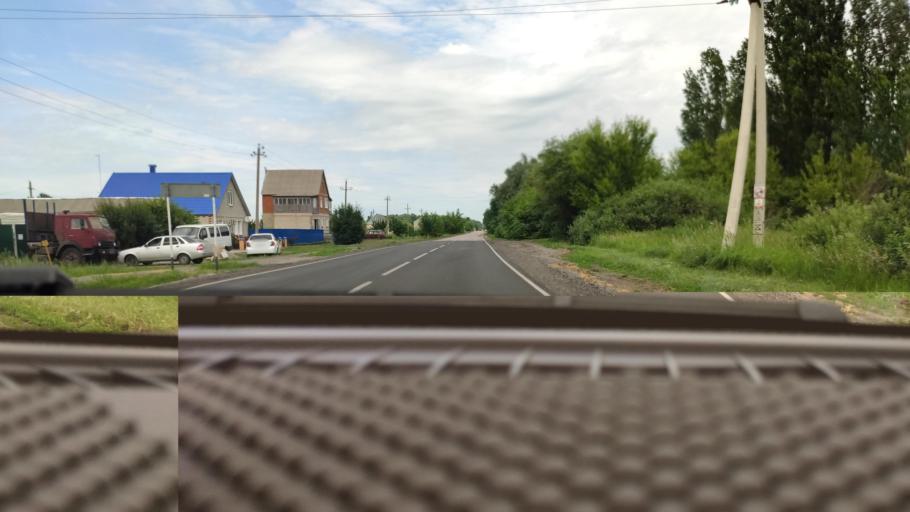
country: RU
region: Voronezj
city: Panino
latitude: 51.6497
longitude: 40.1127
